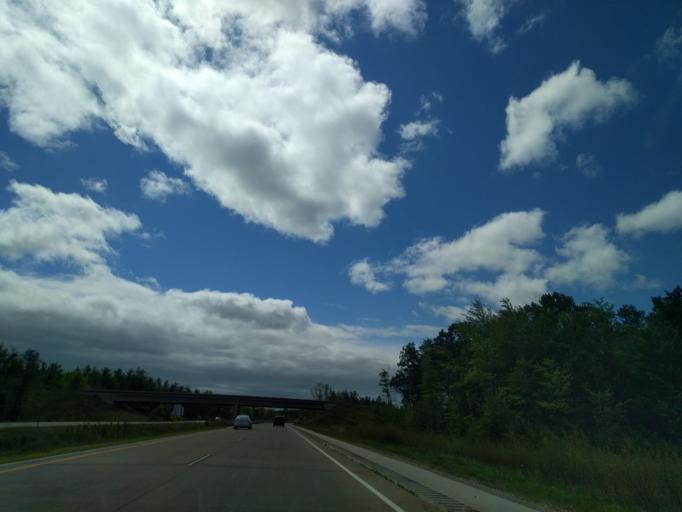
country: US
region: Wisconsin
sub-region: Oconto County
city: Oconto
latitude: 44.8757
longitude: -87.8953
